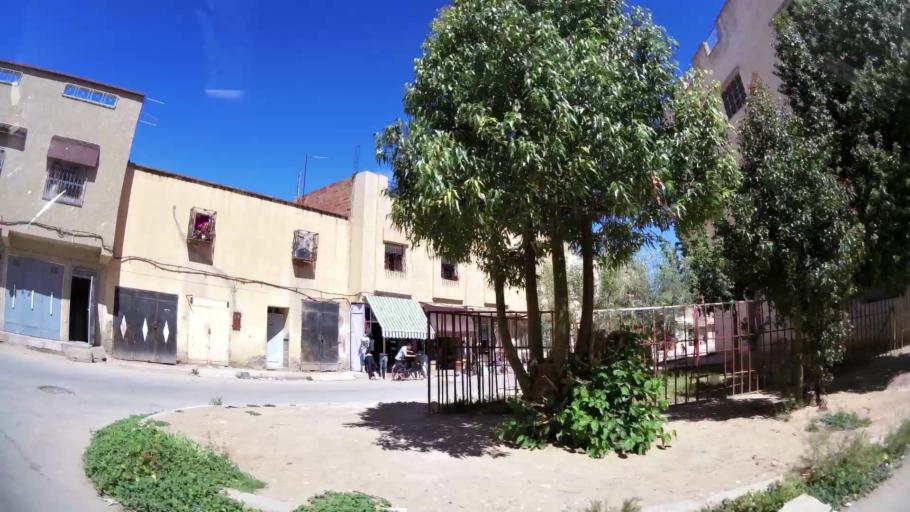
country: MA
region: Oriental
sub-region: Oujda-Angad
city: Oujda
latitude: 34.6681
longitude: -1.9349
